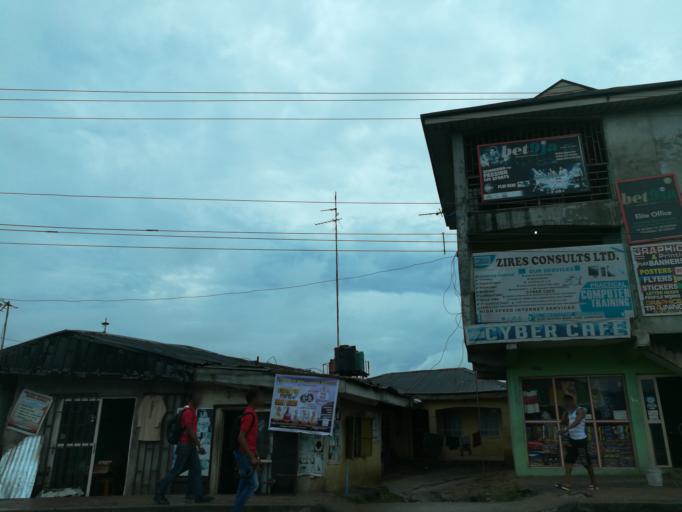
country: NG
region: Rivers
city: Port Harcourt
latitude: 4.8553
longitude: 7.0314
